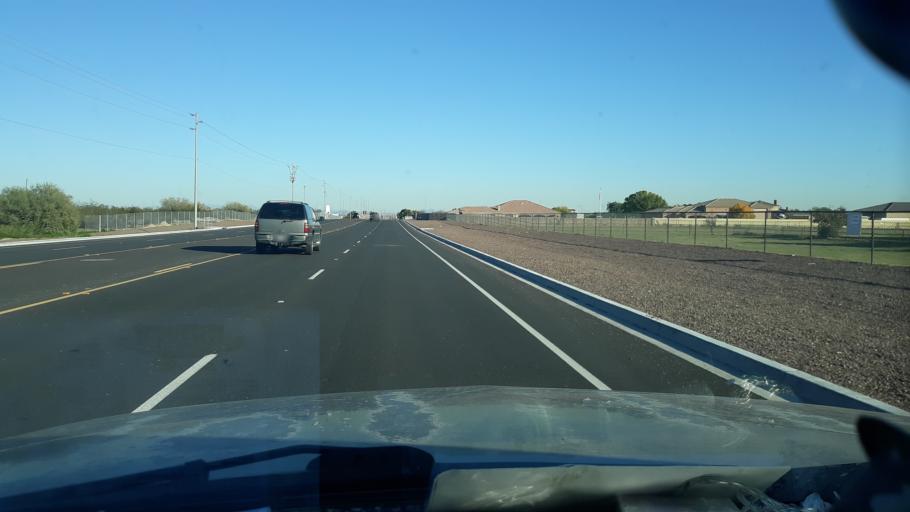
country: US
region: Arizona
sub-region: Maricopa County
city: Citrus Park
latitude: 33.5662
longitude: -112.4399
